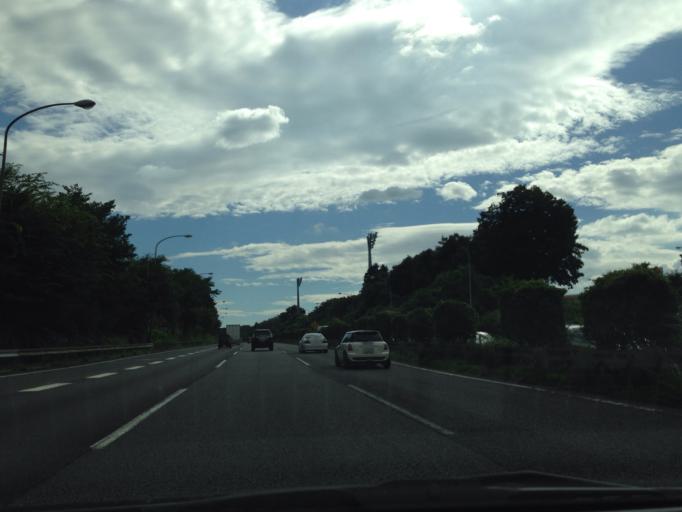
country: JP
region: Shizuoka
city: Gotemba
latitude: 35.3159
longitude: 138.9676
